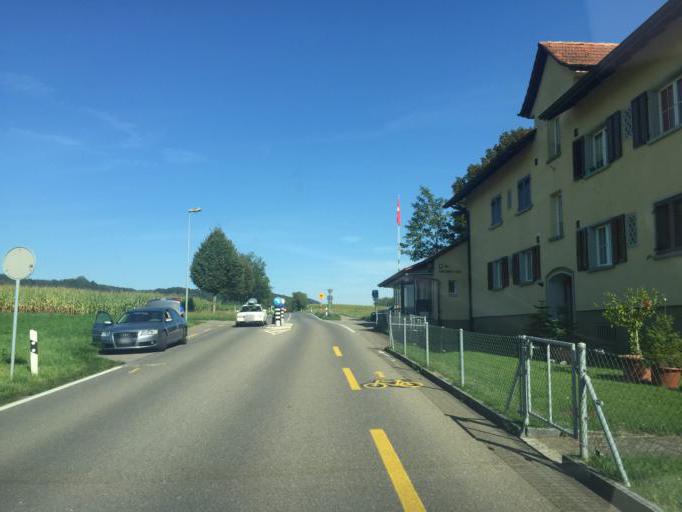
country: CH
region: Thurgau
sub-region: Frauenfeld District
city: Diessenhofen
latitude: 47.6951
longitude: 8.7261
